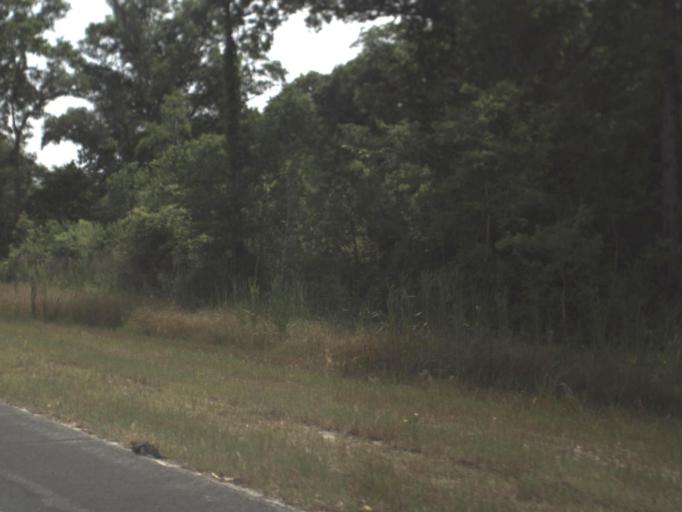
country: US
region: Florida
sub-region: Nassau County
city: Callahan
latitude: 30.5395
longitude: -81.8526
